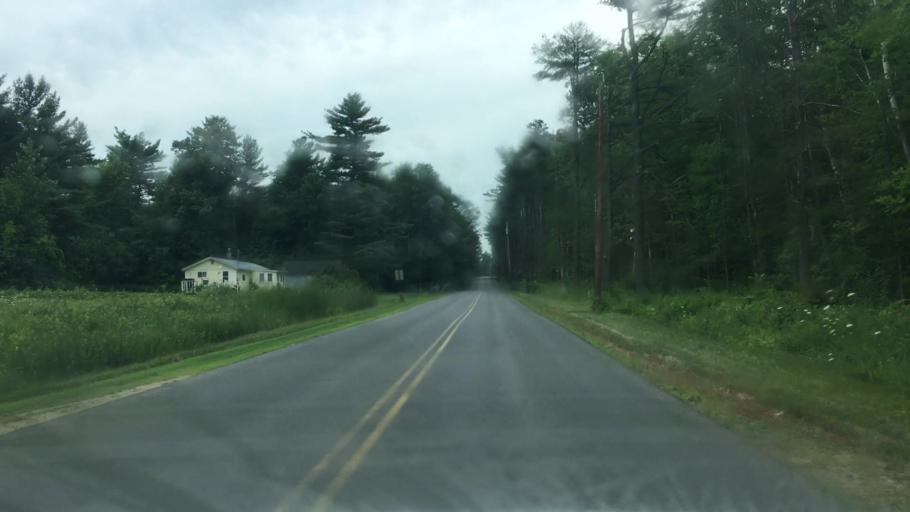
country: US
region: New York
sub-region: Clinton County
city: Morrisonville
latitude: 44.6424
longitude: -73.5728
